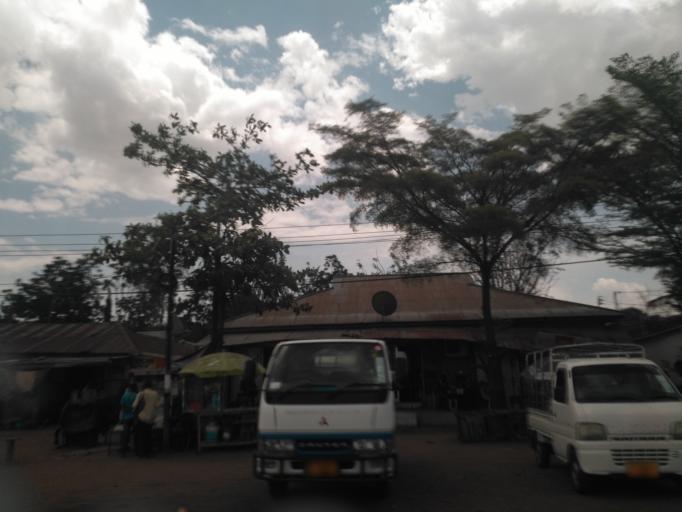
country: TZ
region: Mwanza
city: Mwanza
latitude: -2.6024
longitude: 32.9314
